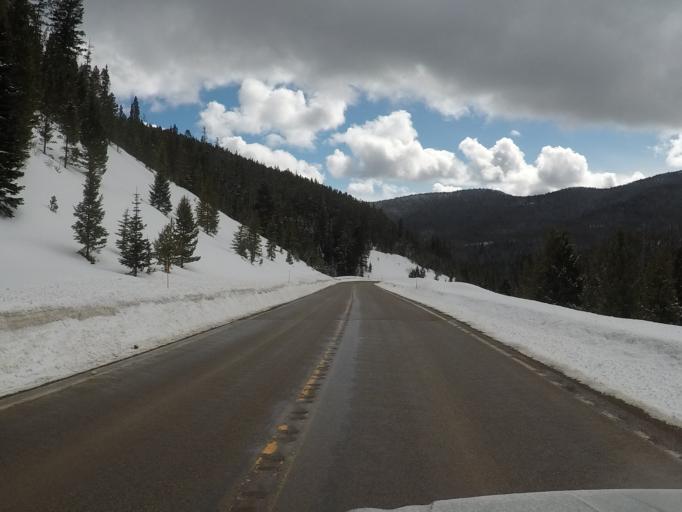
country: US
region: Montana
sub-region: Meagher County
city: White Sulphur Springs
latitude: 46.8168
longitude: -110.7029
